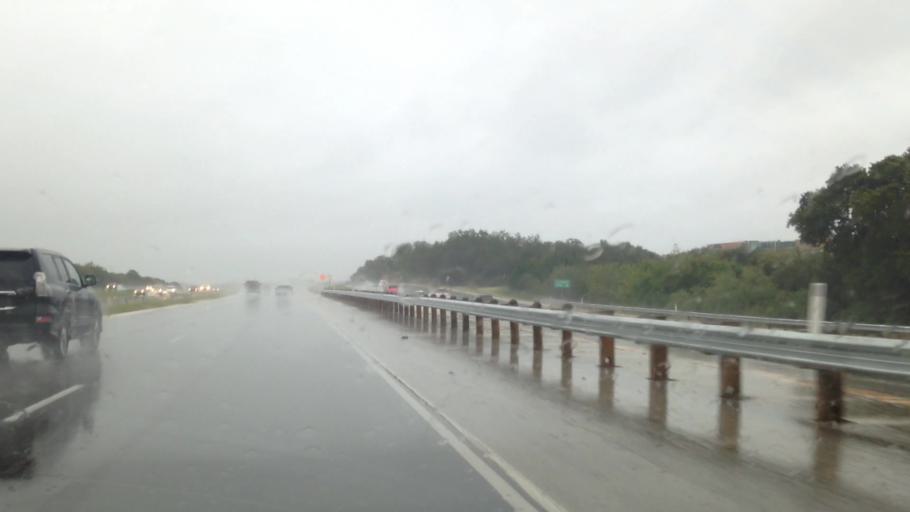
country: US
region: Texas
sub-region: Bexar County
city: Shavano Park
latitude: 29.6010
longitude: -98.5565
